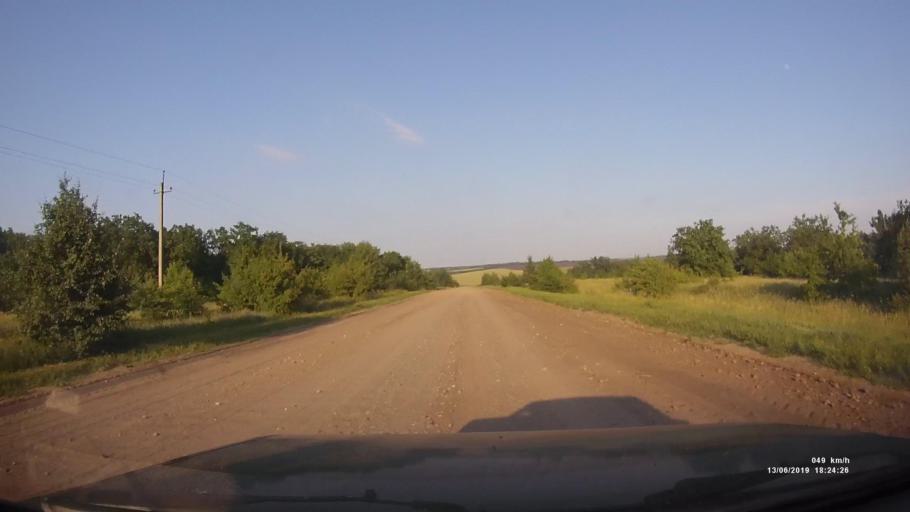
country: RU
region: Rostov
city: Kazanskaya
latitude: 49.8519
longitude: 41.2897
